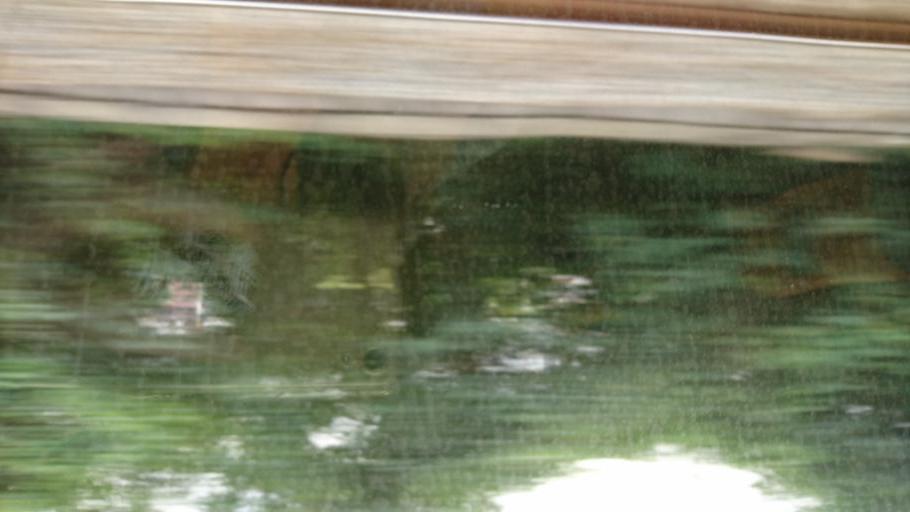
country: TW
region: Taiwan
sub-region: Hsinchu
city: Zhubei
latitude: 24.8563
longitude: 121.0046
